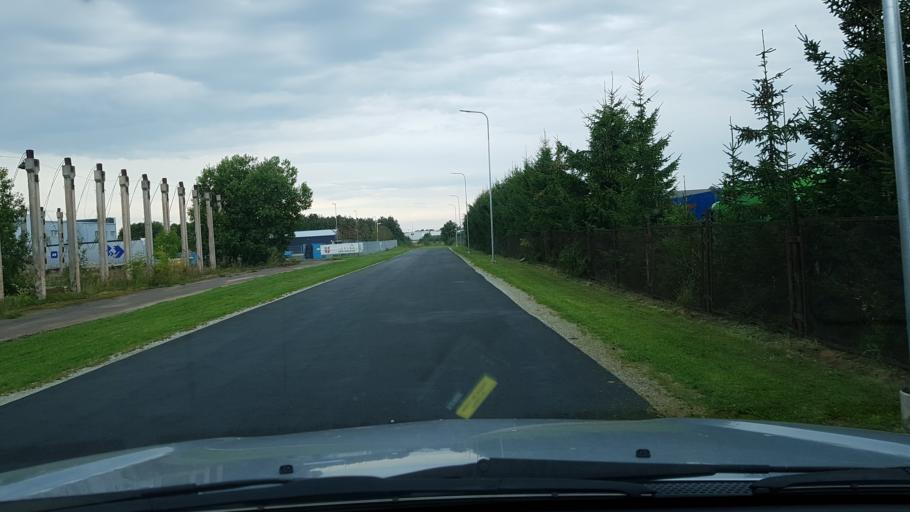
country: EE
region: Harju
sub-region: Rae vald
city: Jueri
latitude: 59.3574
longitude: 24.9000
